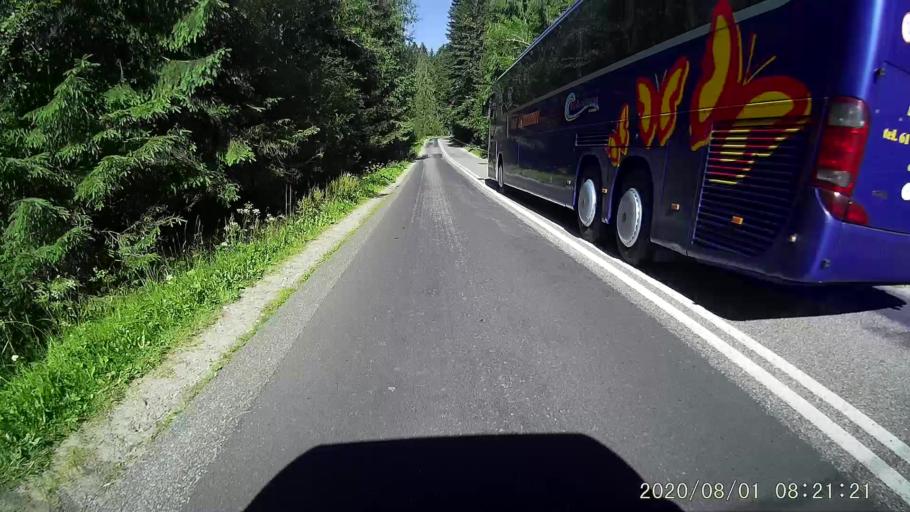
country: PL
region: Lesser Poland Voivodeship
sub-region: Powiat tatrzanski
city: Bukowina Tatrzanska
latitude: 49.2886
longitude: 20.0840
